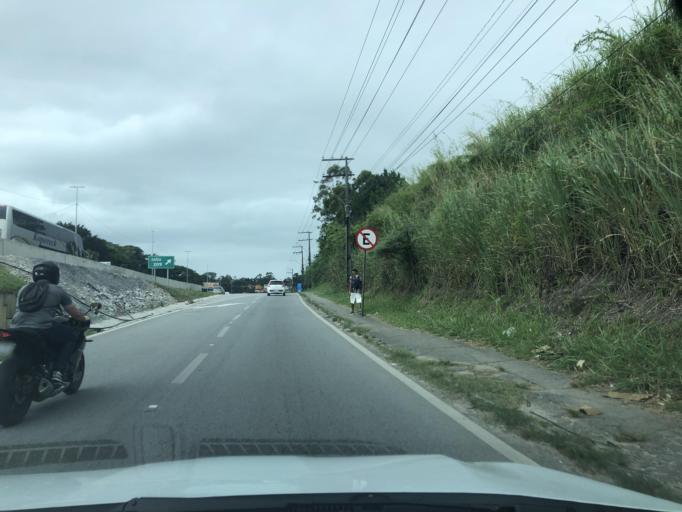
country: BR
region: Santa Catarina
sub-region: Sao Jose
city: Campinas
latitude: -27.6058
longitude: -48.6343
